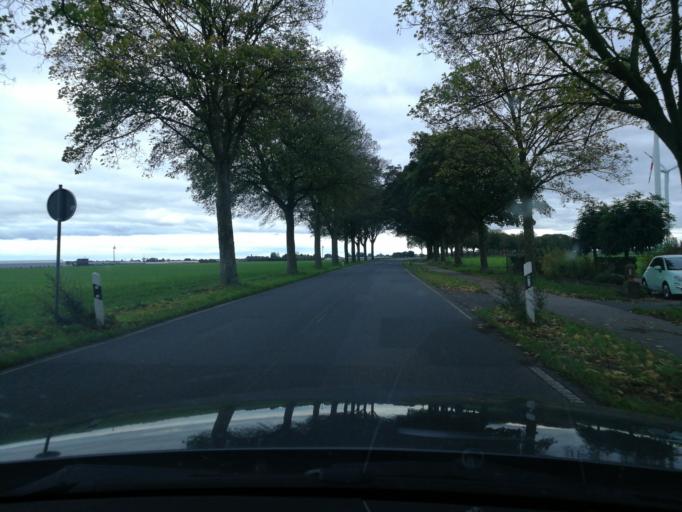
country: NL
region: Limburg
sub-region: Gemeente Venlo
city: Arcen
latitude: 51.4724
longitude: 6.2267
